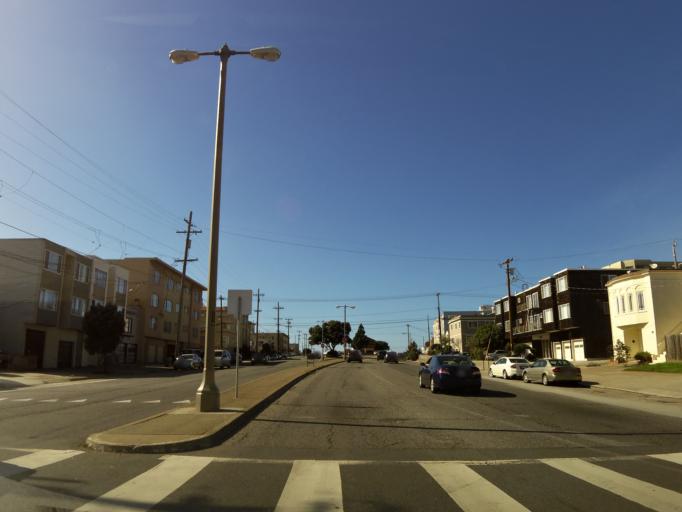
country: US
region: California
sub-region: San Francisco County
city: San Francisco
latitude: 37.7794
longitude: -122.4998
